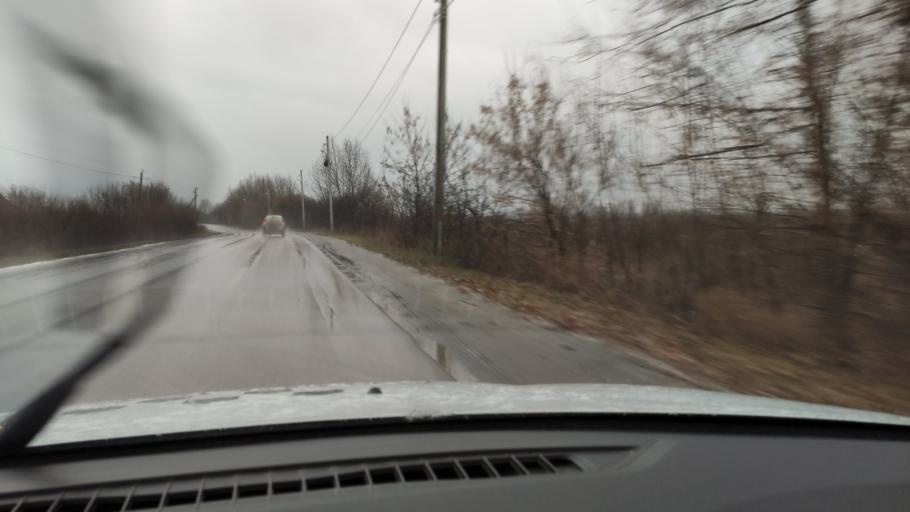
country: RU
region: Perm
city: Kondratovo
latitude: 57.9716
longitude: 56.1131
